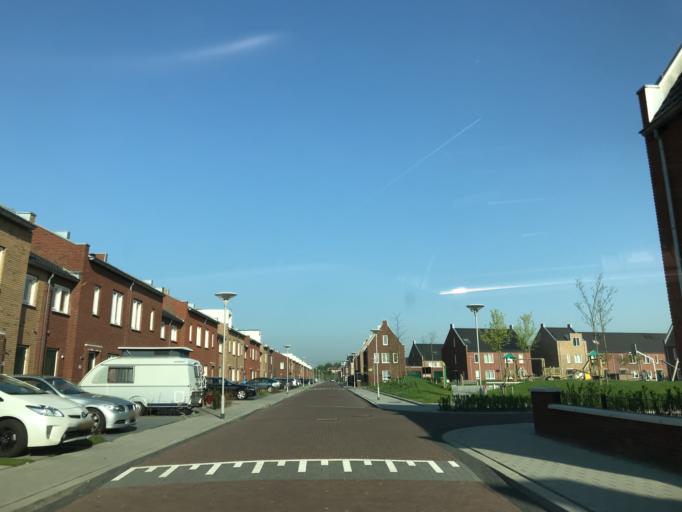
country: NL
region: North Holland
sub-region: Gemeente Diemen
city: Diemen
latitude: 52.3340
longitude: 4.9722
